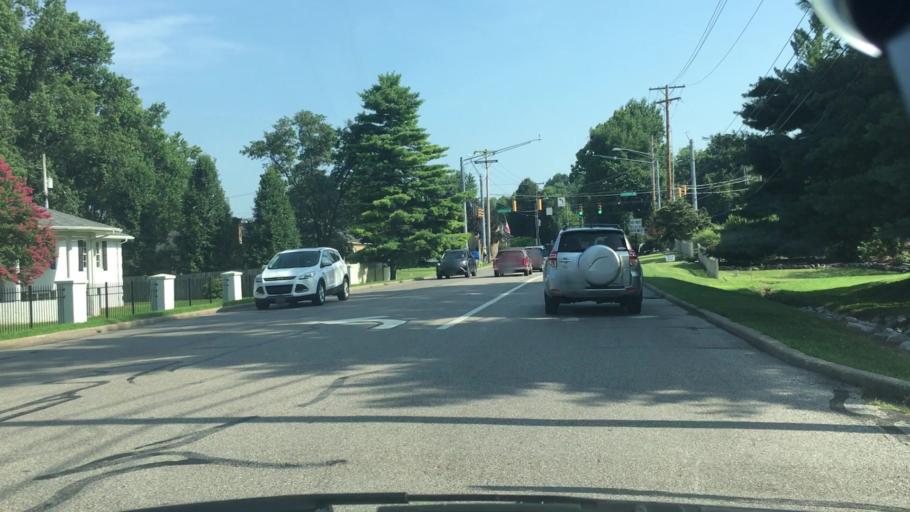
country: US
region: Indiana
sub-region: Vanderburgh County
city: Melody Hill
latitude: 37.9703
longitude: -87.4744
